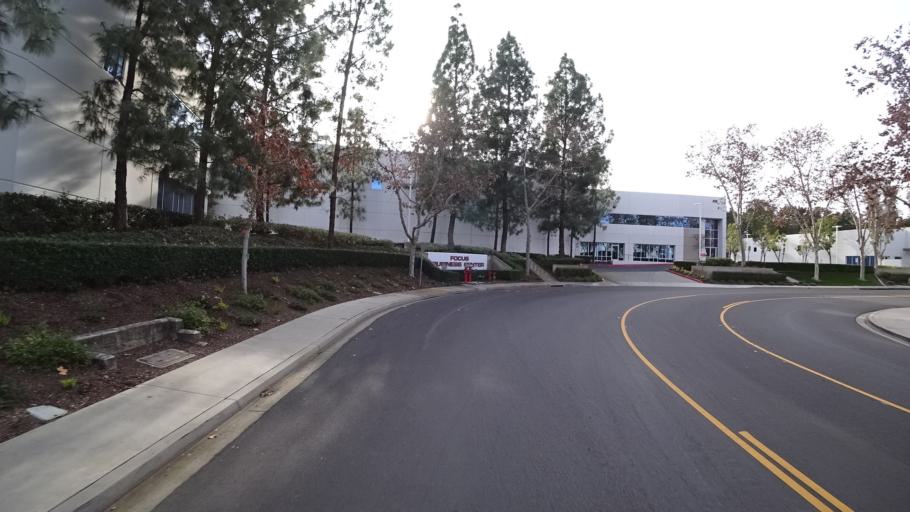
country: US
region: California
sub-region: Orange County
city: Aliso Viejo
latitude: 33.5657
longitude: -117.7259
